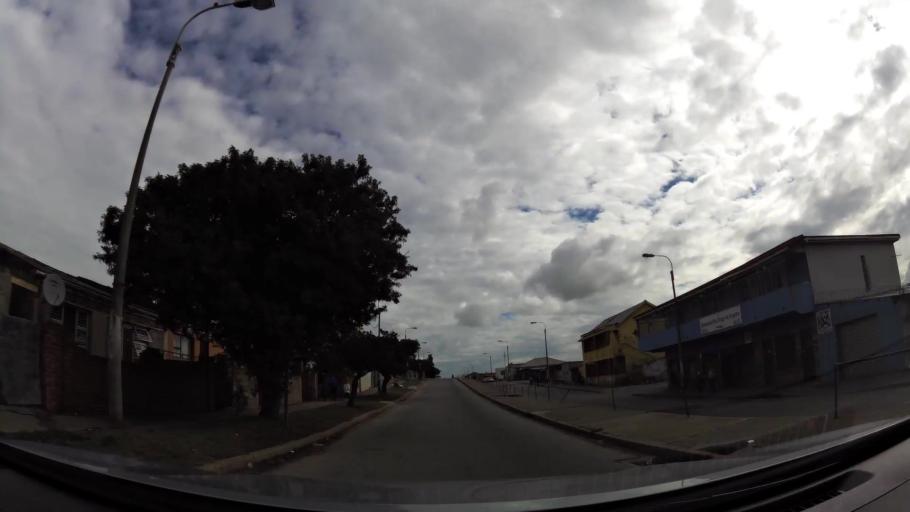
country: ZA
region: Eastern Cape
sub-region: Nelson Mandela Bay Metropolitan Municipality
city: Port Elizabeth
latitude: -33.9353
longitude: 25.5791
